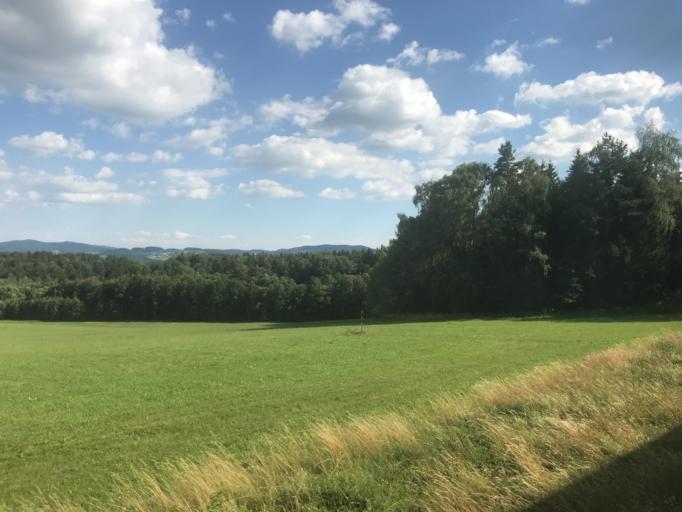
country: CZ
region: Jihocesky
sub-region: Okres Cesky Krumlov
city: Dolni Dvoriste
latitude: 48.6735
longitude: 14.4441
